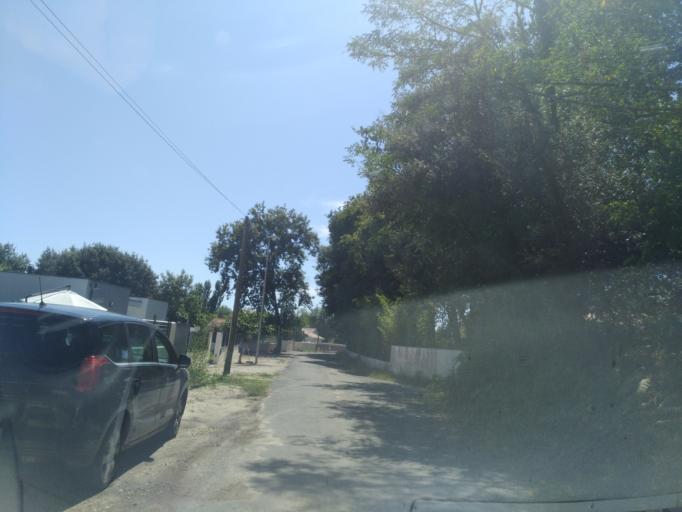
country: FR
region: Poitou-Charentes
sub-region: Departement de la Charente-Maritime
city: Saint-Palais-sur-Mer
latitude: 45.6601
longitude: -1.0768
